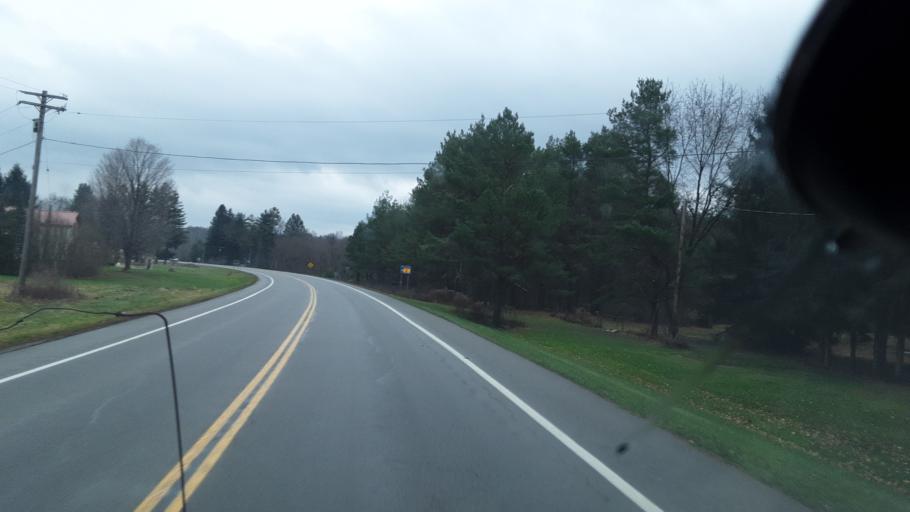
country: US
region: New York
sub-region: Allegany County
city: Houghton
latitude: 42.3865
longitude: -78.2387
